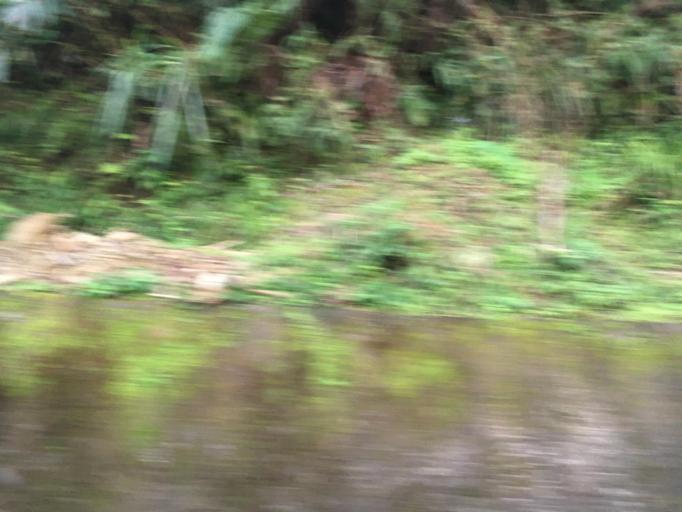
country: TW
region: Taiwan
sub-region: Yilan
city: Yilan
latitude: 24.7551
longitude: 121.5967
